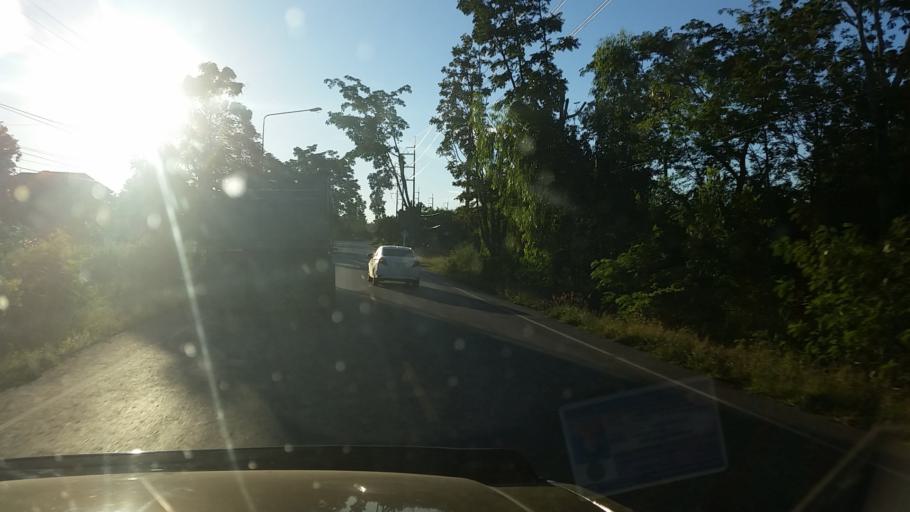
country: TH
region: Chaiyaphum
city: Sap Yai
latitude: 15.6771
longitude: 101.6879
